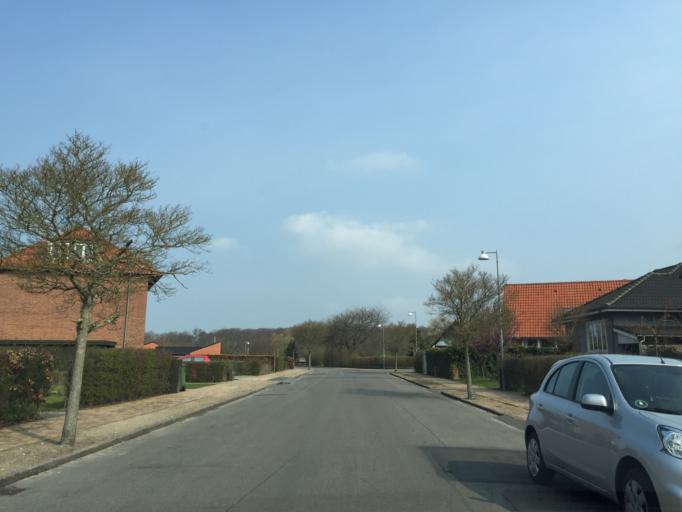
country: DK
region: South Denmark
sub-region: Odense Kommune
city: Odense
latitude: 55.4179
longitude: 10.3922
